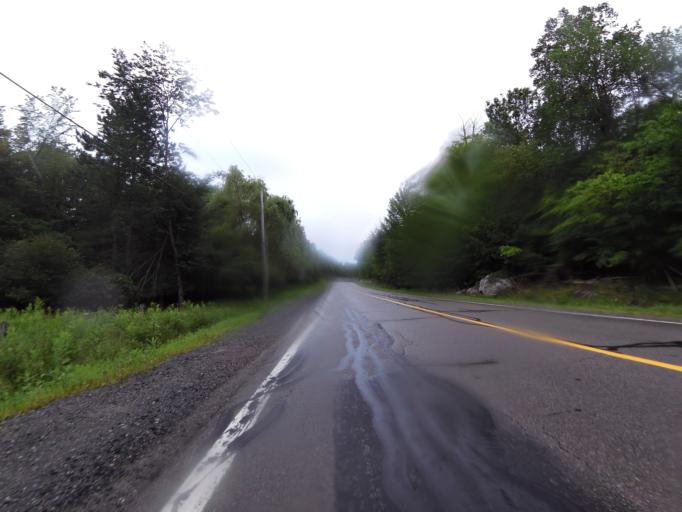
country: CA
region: Ontario
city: Perth
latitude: 44.9878
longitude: -76.3945
